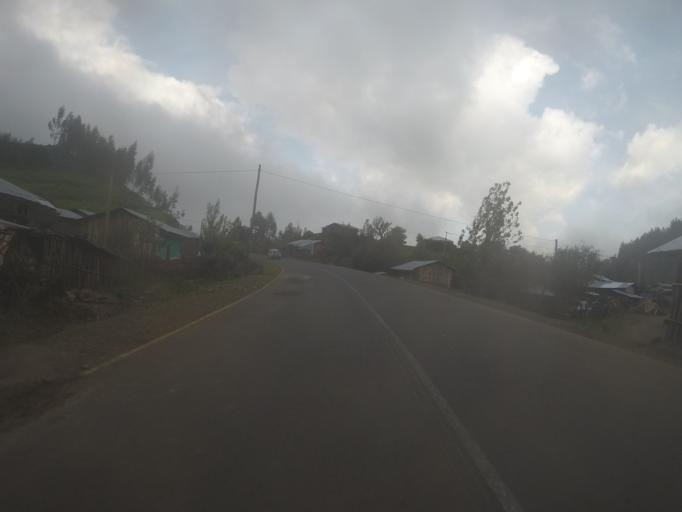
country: ET
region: Amhara
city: Gondar
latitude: 12.7243
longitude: 37.5100
